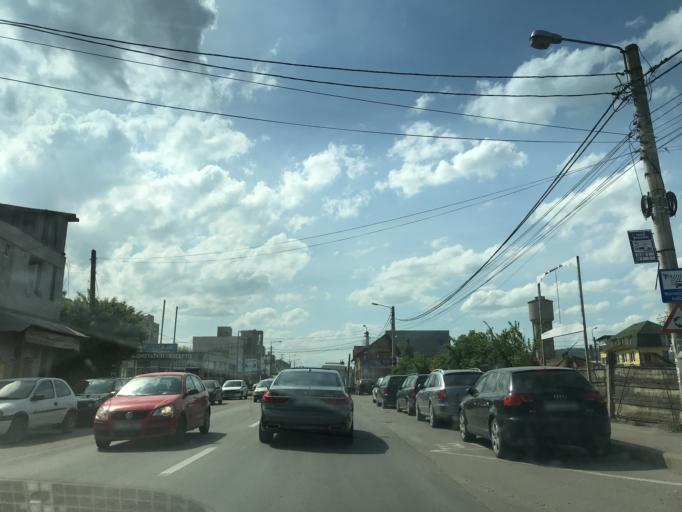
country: RO
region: Cluj
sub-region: Municipiul Cluj-Napoca
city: Cluj-Napoca
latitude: 46.7877
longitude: 23.6285
